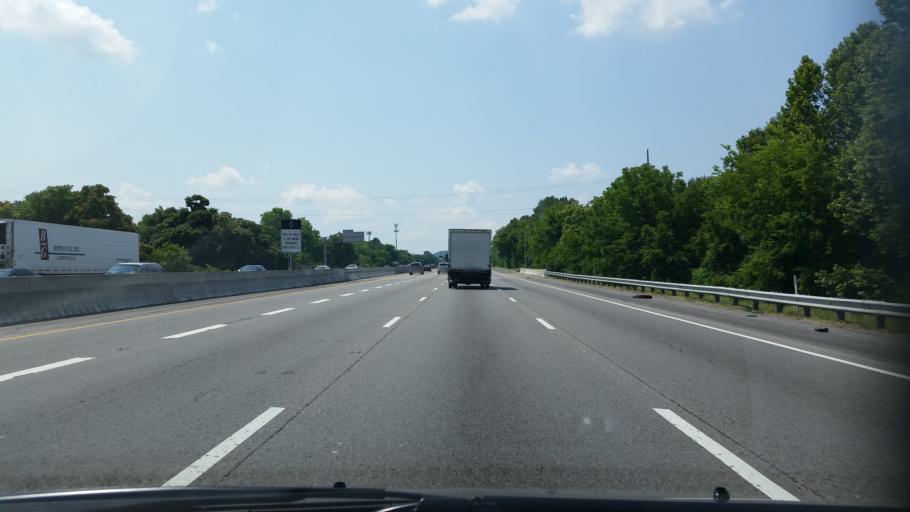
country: US
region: Tennessee
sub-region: Davidson County
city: Oak Hill
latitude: 36.0673
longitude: -86.7708
